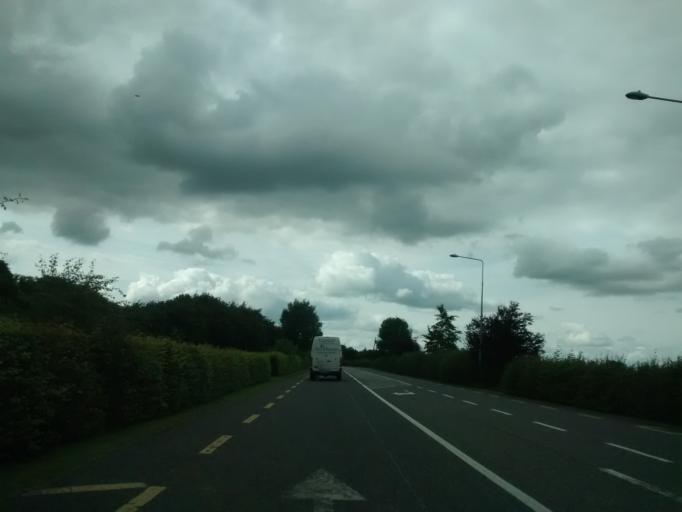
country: IE
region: Leinster
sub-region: An Iarmhi
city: Moate
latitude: 53.3775
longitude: -7.6618
